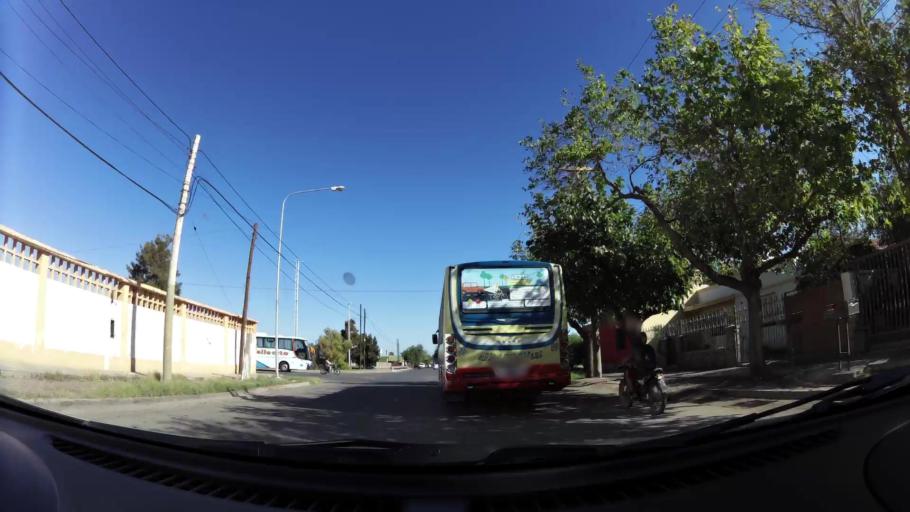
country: AR
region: San Juan
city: San Juan
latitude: -31.5153
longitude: -68.5244
